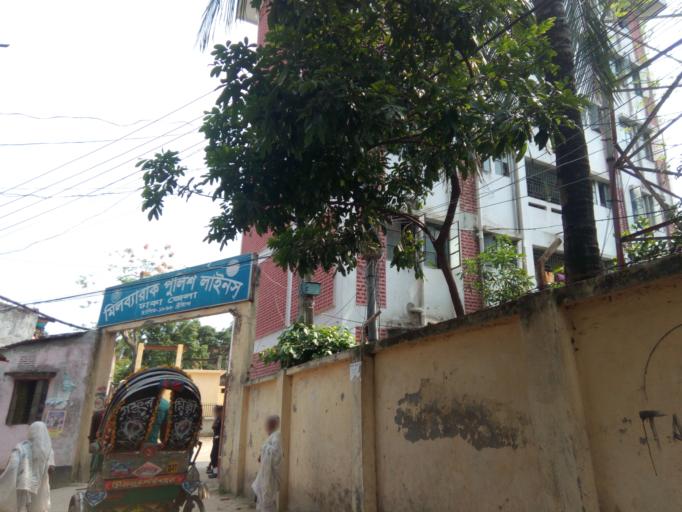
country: BD
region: Dhaka
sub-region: Dhaka
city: Dhaka
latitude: 23.7013
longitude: 90.4189
